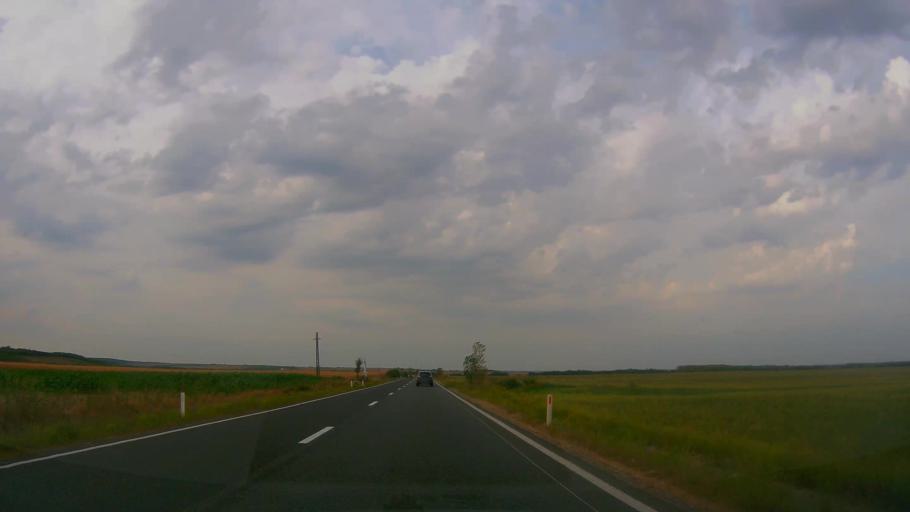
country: RO
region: Satu Mare
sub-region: Comuna Beltiug
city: Beltiug
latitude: 47.5753
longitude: 22.8783
